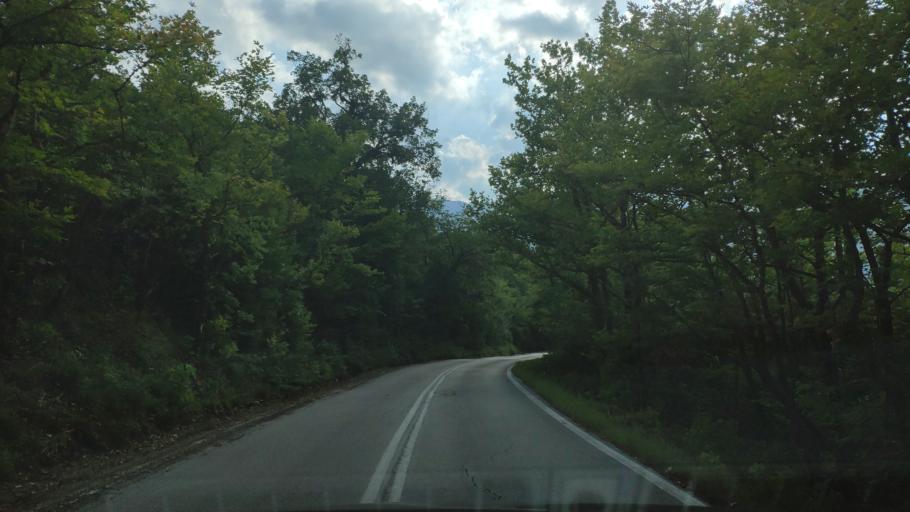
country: GR
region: Epirus
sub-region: Nomos Artas
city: Agios Dimitrios
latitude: 39.4594
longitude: 21.0619
